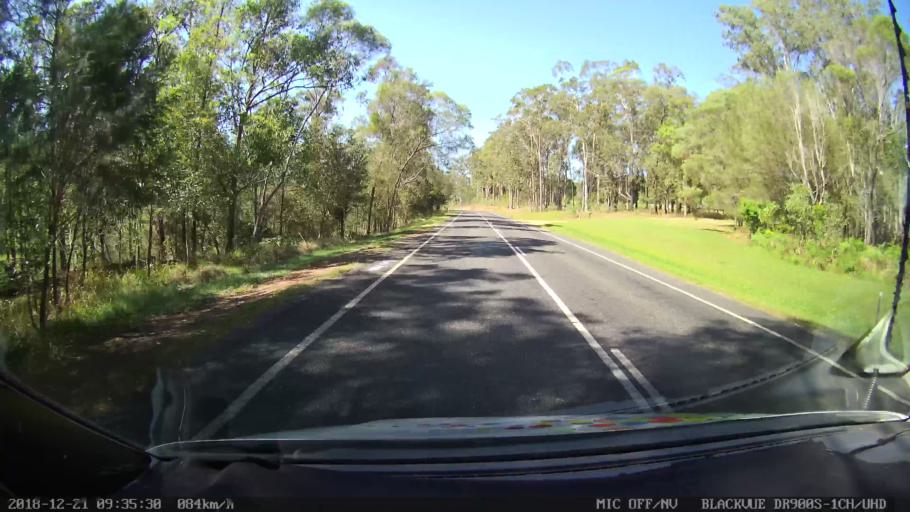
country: AU
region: New South Wales
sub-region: Clarence Valley
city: Grafton
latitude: -29.5116
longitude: 152.9810
